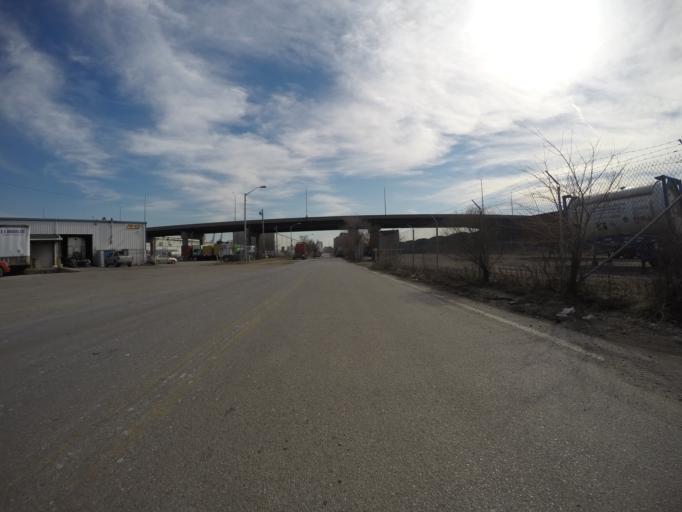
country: US
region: Maryland
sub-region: Baltimore County
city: Dundalk
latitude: 39.2681
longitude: -76.5555
